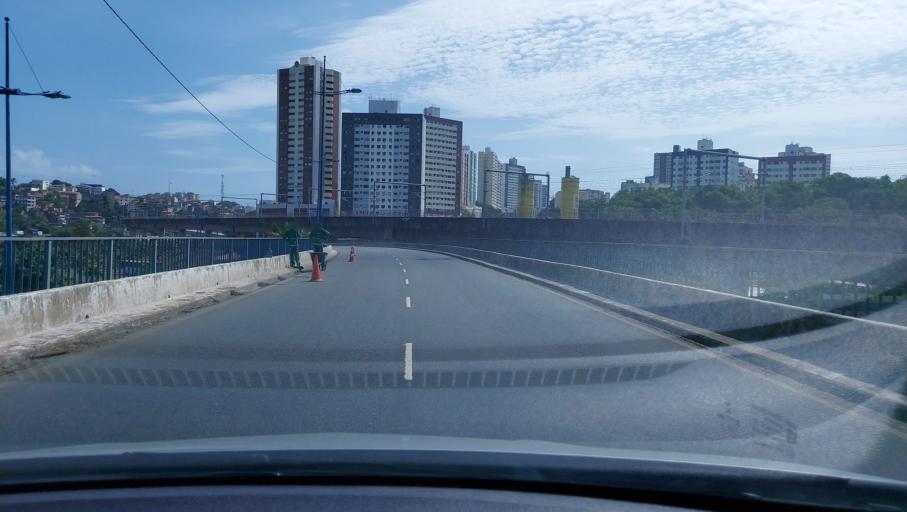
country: BR
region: Bahia
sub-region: Salvador
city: Salvador
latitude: -12.9715
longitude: -38.4770
